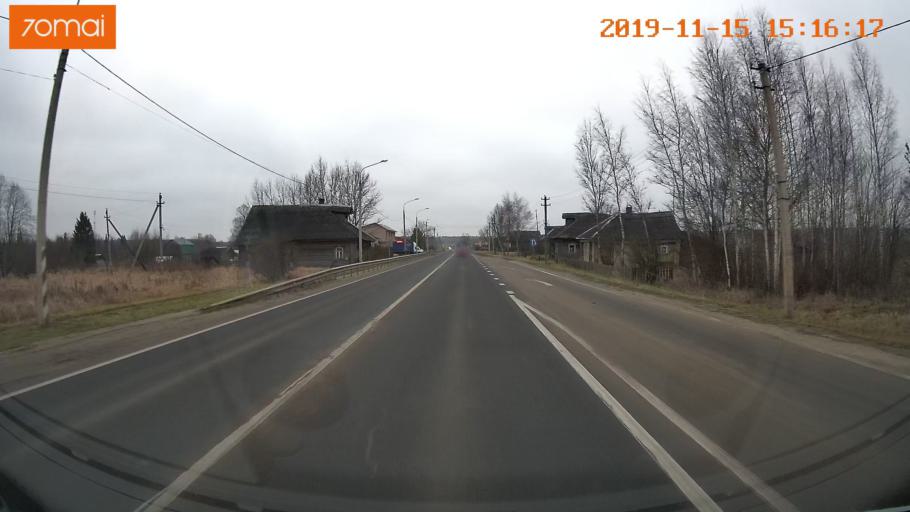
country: RU
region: Jaroslavl
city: Danilov
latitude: 58.2742
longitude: 40.1924
